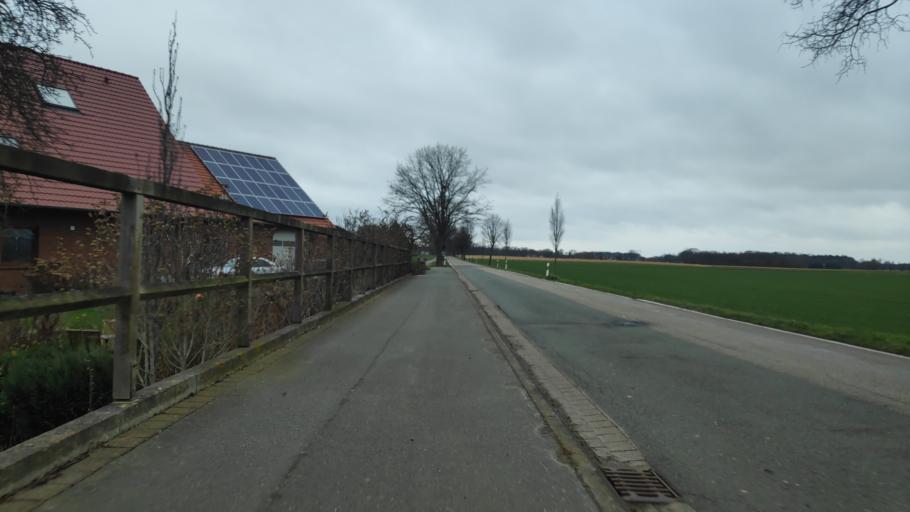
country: DE
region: North Rhine-Westphalia
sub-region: Regierungsbezirk Detmold
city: Hille
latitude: 52.3439
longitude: 8.7963
